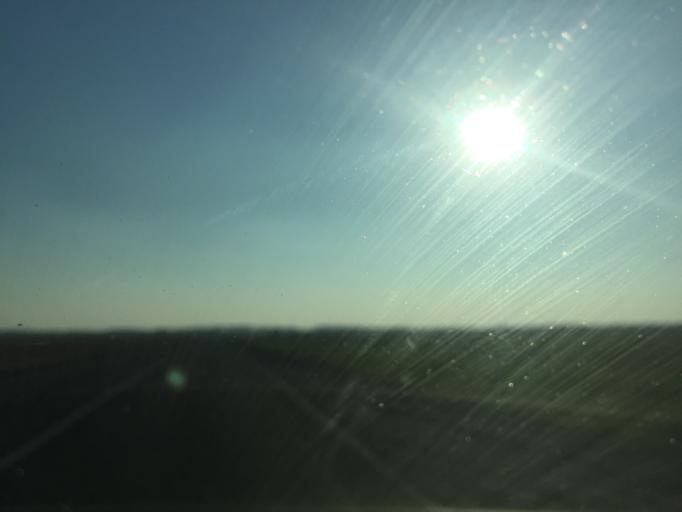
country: BY
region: Gomel
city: Dobrush
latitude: 52.3159
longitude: 31.2446
